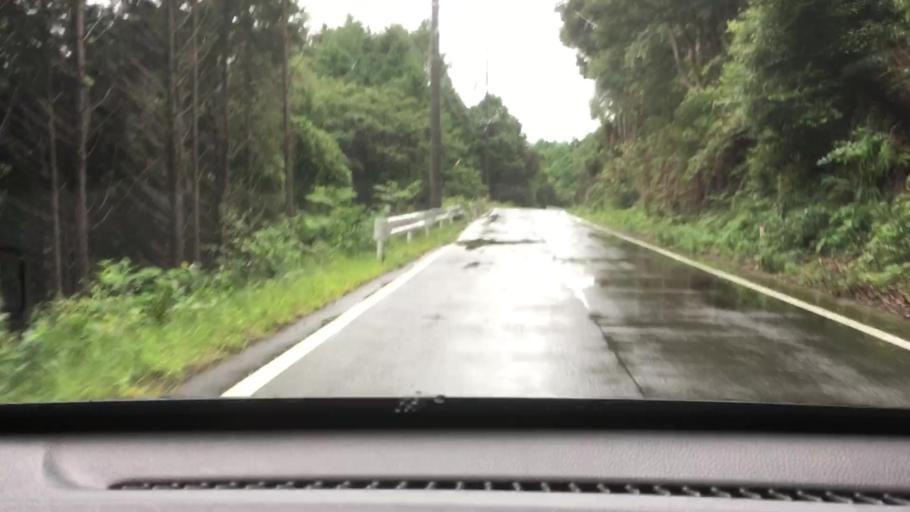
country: JP
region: Nagasaki
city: Togitsu
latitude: 32.8726
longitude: 129.7640
